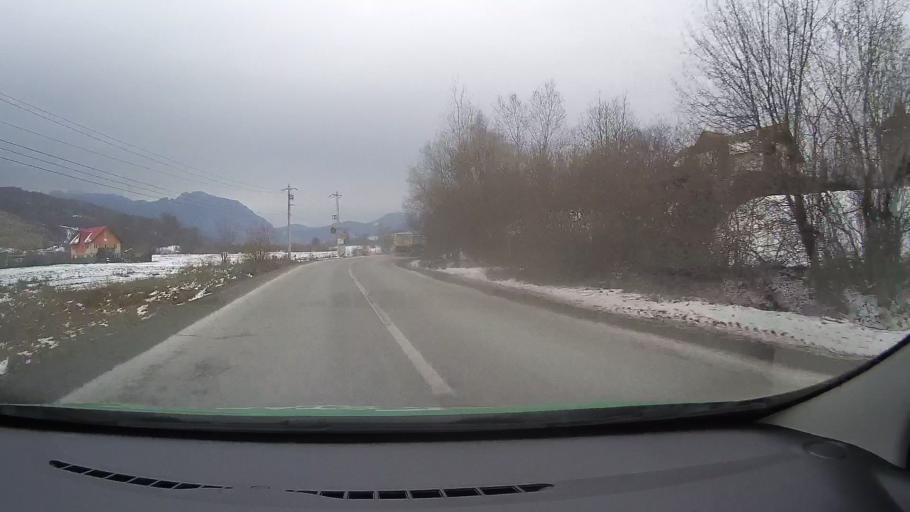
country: RO
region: Brasov
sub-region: Oras Rasnov
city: Rasnov
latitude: 45.5633
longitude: 25.4608
